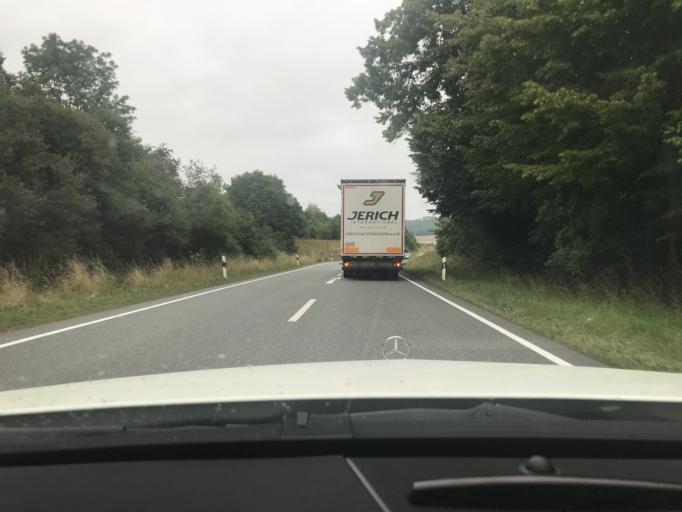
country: DE
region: Thuringia
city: Worbis
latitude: 51.4100
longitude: 10.3506
